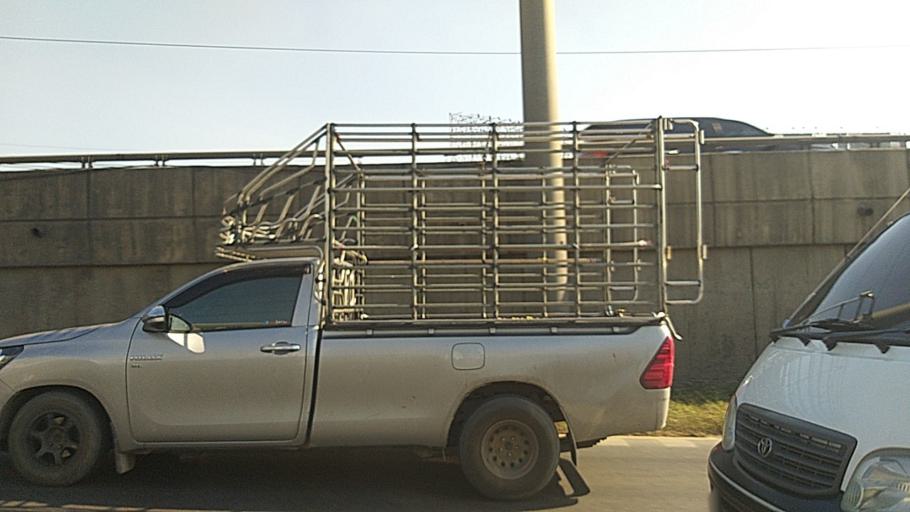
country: TH
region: Bangkok
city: Sai Mai
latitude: 13.9851
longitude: 100.6196
